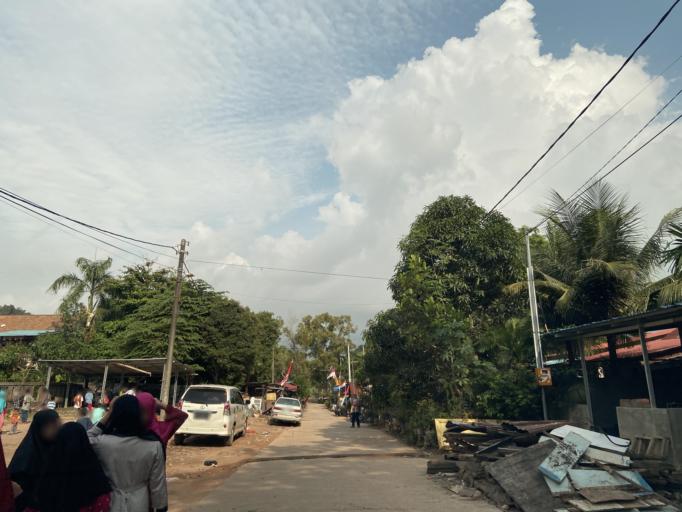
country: SG
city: Singapore
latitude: 1.1238
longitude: 104.0139
